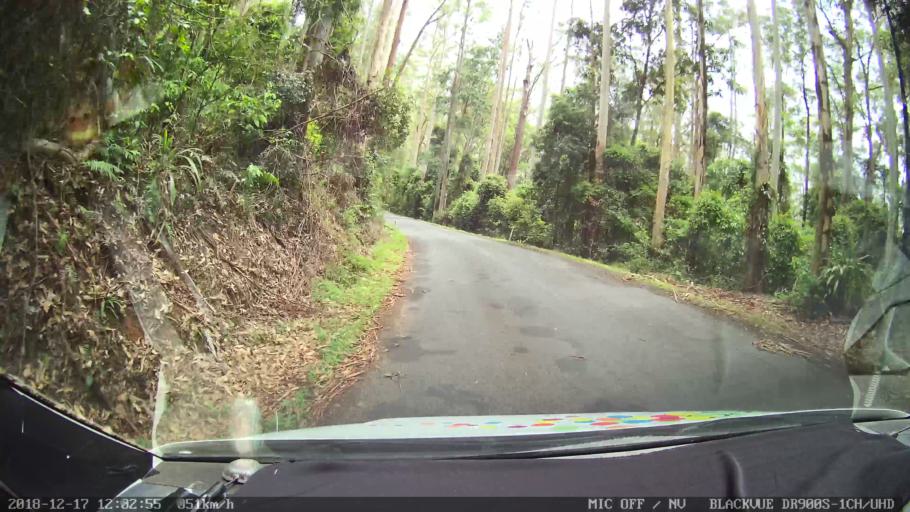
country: AU
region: New South Wales
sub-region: Kyogle
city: Kyogle
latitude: -28.5123
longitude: 152.5695
